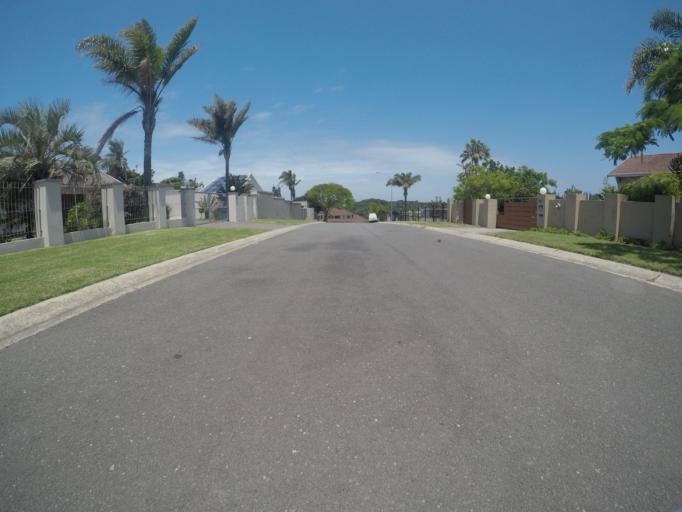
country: ZA
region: Eastern Cape
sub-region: Buffalo City Metropolitan Municipality
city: East London
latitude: -33.0035
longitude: 27.9226
